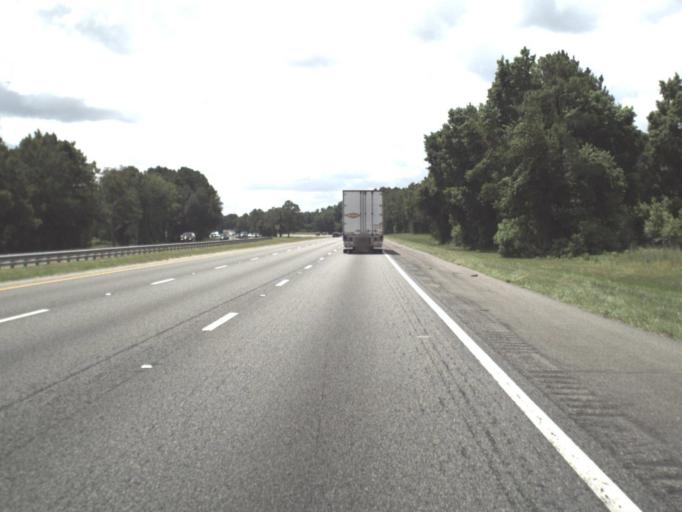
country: US
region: Florida
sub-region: Suwannee County
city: Wellborn
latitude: 30.2453
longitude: -82.7425
